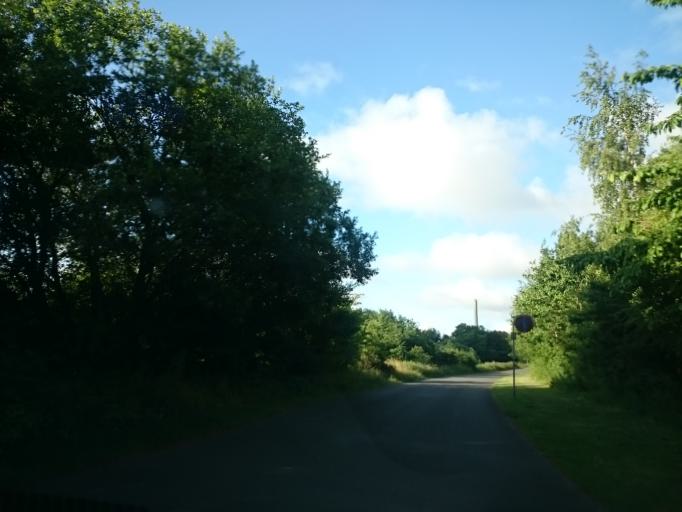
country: DK
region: Central Jutland
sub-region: Arhus Kommune
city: Stavtrup
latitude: 56.1123
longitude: 10.1062
